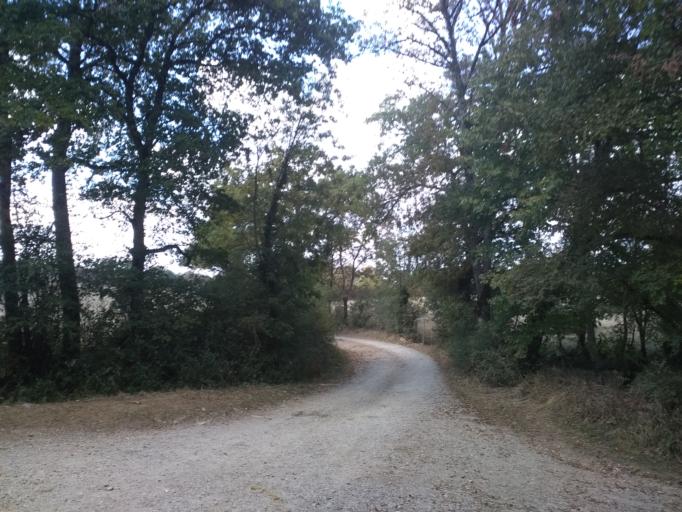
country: FR
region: Midi-Pyrenees
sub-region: Departement de l'Aveyron
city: Bozouls
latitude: 44.4598
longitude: 2.6769
